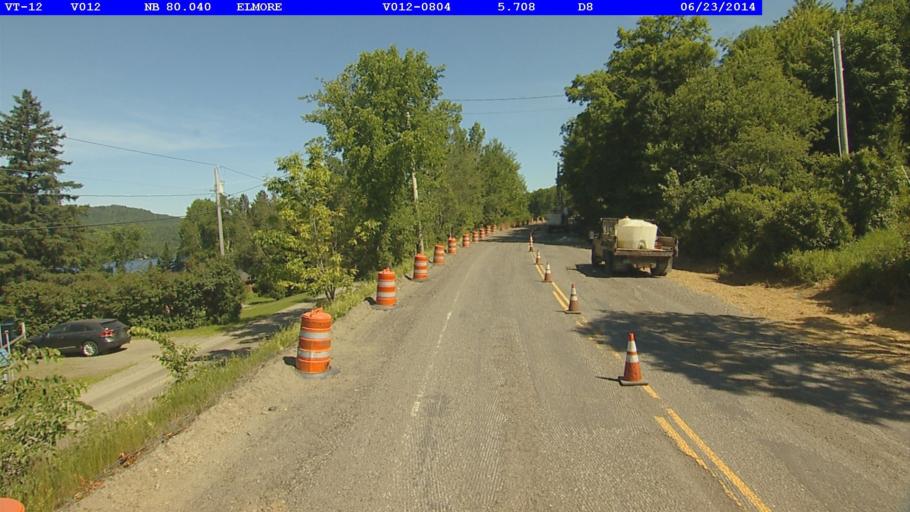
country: US
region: Vermont
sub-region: Lamoille County
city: Morrisville
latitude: 44.5265
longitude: -72.5185
